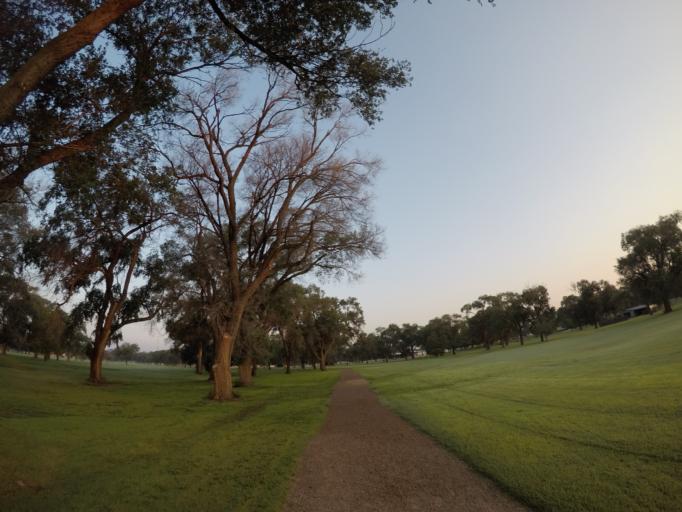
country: US
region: New Mexico
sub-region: Curry County
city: Clovis
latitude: 34.4061
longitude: -103.1800
